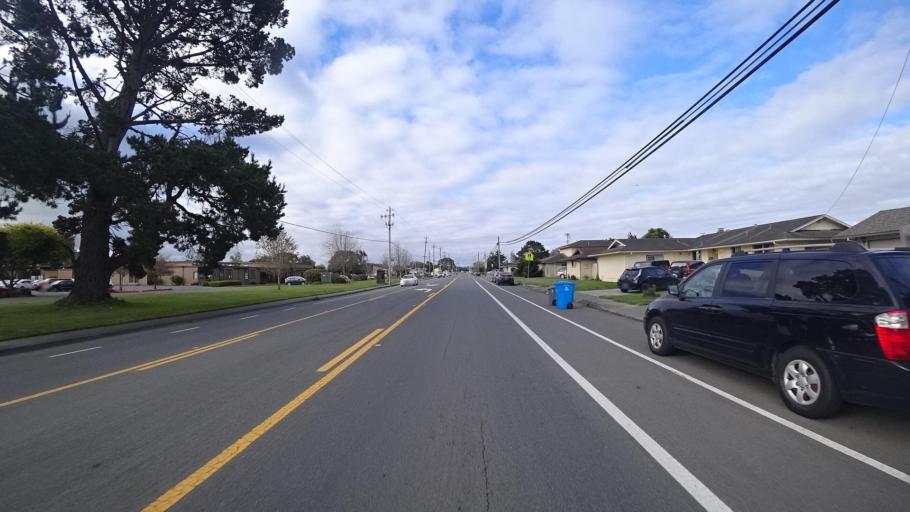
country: US
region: California
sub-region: Humboldt County
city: Arcata
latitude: 40.8972
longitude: -124.0930
